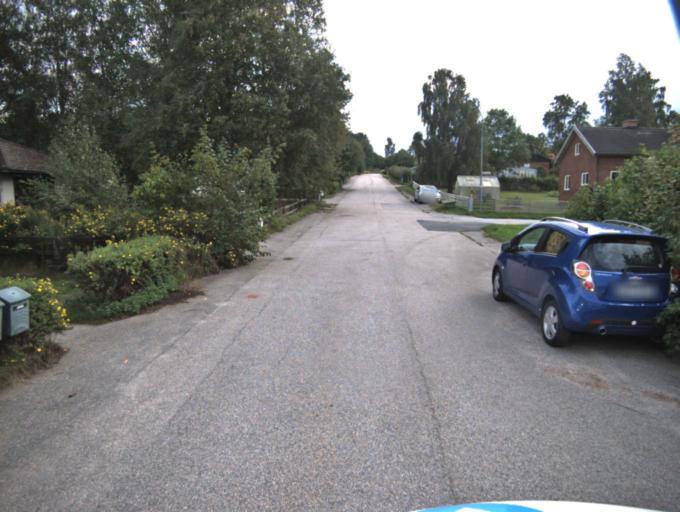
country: SE
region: Vaestra Goetaland
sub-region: Ulricehamns Kommun
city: Ulricehamn
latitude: 57.8413
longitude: 13.2874
